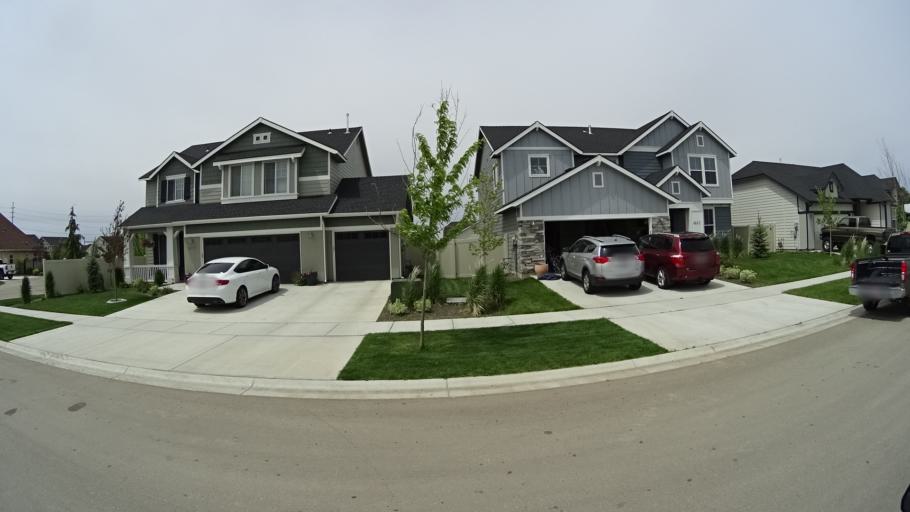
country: US
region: Idaho
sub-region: Ada County
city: Meridian
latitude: 43.5626
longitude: -116.3512
